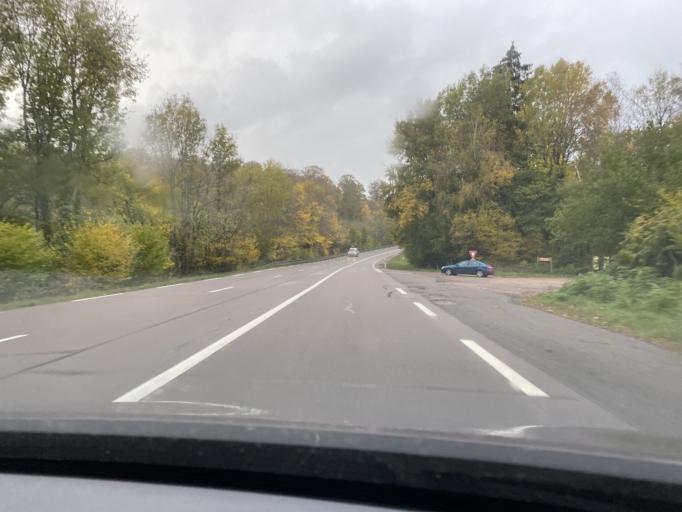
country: FR
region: Bourgogne
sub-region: Departement de la Cote-d'Or
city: Saulieu
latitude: 47.3008
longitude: 4.2115
